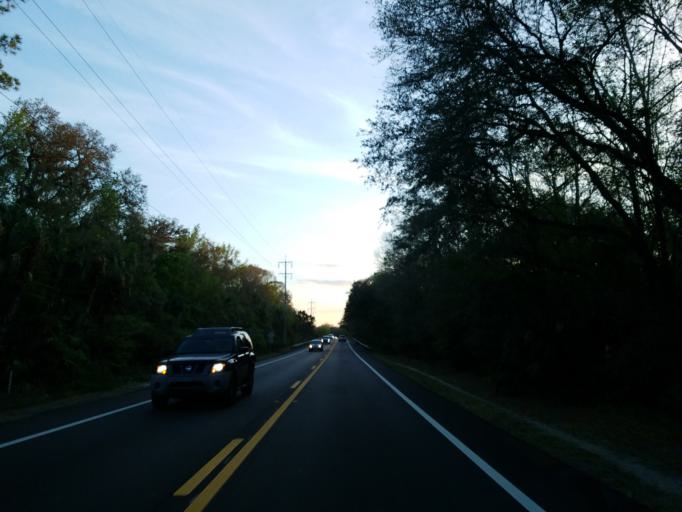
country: US
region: Florida
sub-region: Hillsborough County
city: Thonotosassa
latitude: 28.1012
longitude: -82.3096
